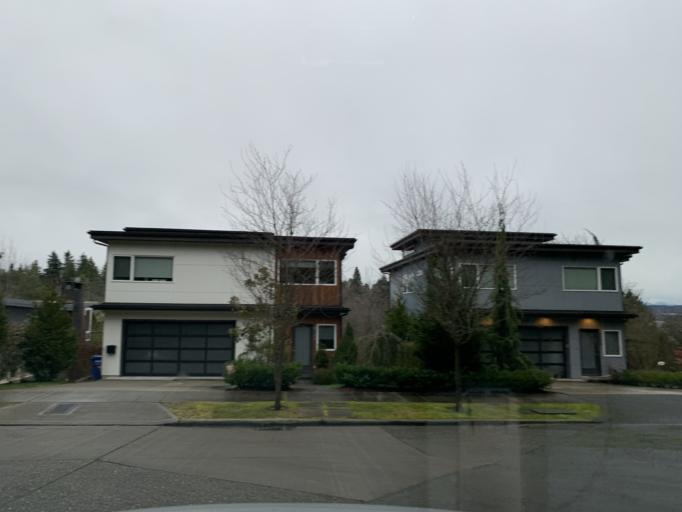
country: US
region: Washington
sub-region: King County
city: Yarrow Point
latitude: 47.6649
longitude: -122.2696
